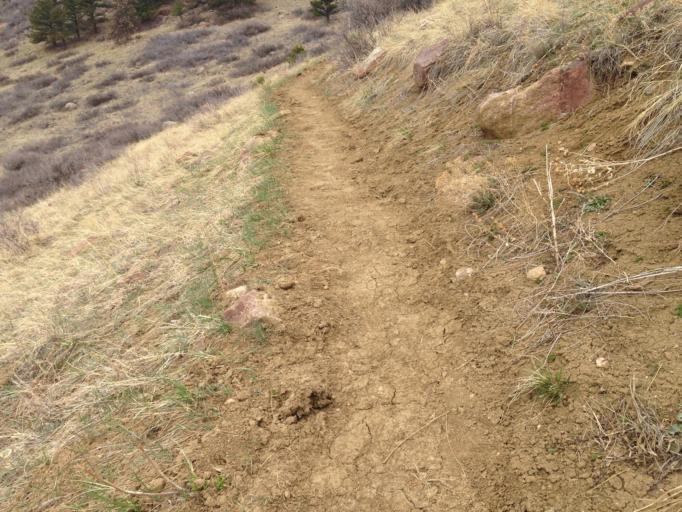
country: US
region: Colorado
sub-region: Boulder County
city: Boulder
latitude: 39.9439
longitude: -105.2705
